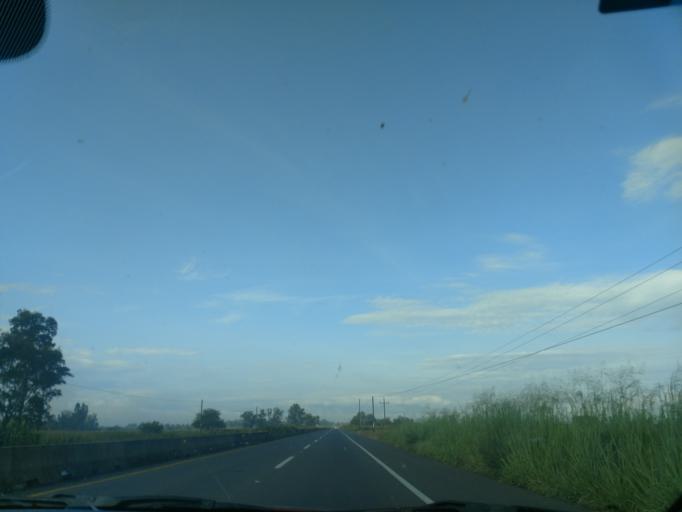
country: MX
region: Jalisco
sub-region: Ameca
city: Los Pocitos
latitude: 20.5453
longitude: -103.9106
